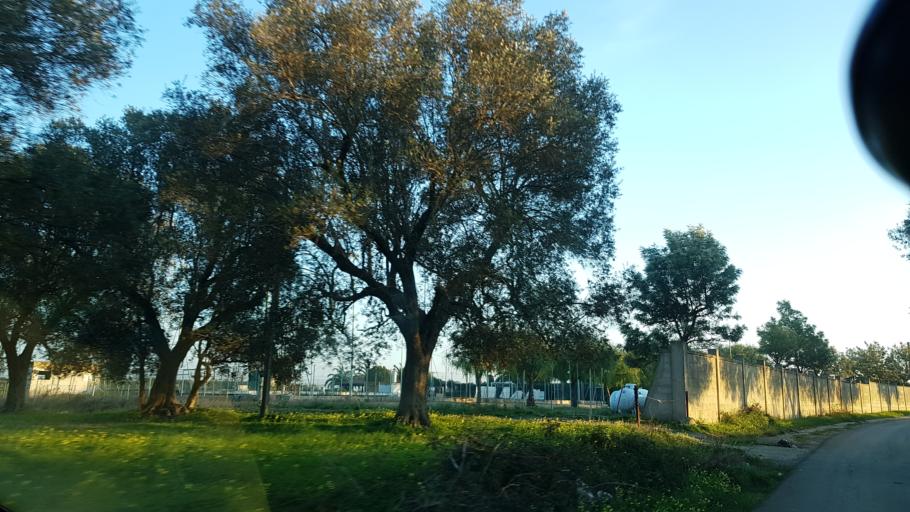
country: IT
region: Apulia
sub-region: Provincia di Brindisi
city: La Rosa
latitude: 40.6114
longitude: 17.9395
